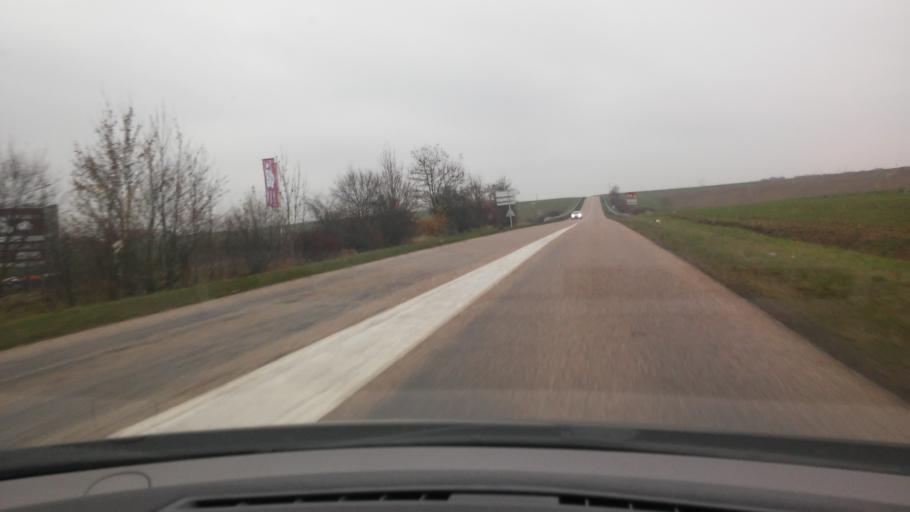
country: FR
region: Lorraine
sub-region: Departement de la Moselle
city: Boulay-Moselle
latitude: 49.1445
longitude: 6.4745
